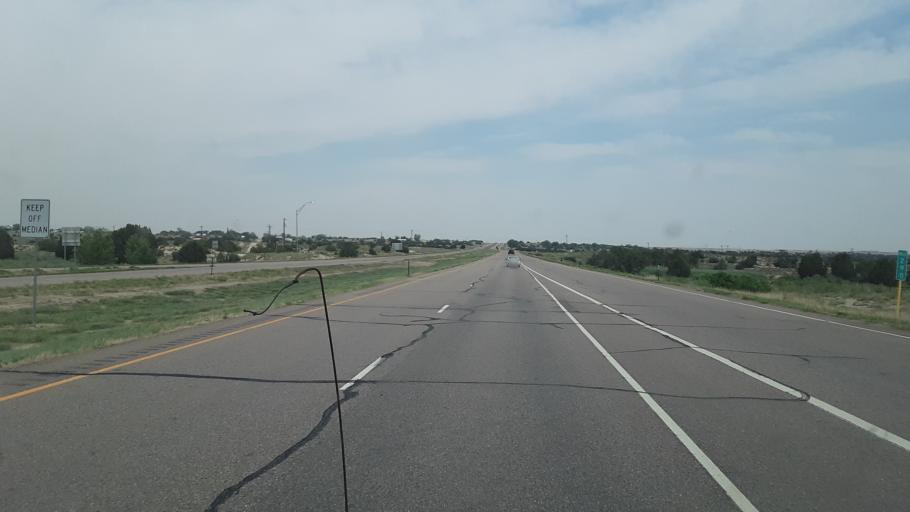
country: US
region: Colorado
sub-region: Fremont County
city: Penrose
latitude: 38.4174
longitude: -105.0383
